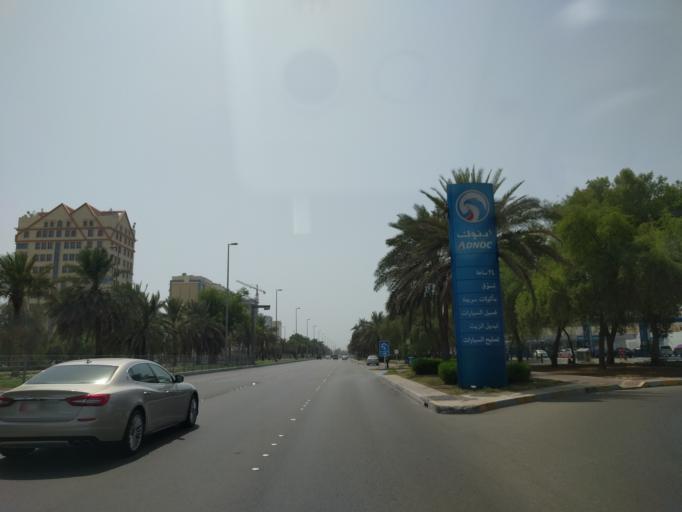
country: AE
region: Abu Dhabi
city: Abu Dhabi
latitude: 24.4387
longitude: 54.4144
